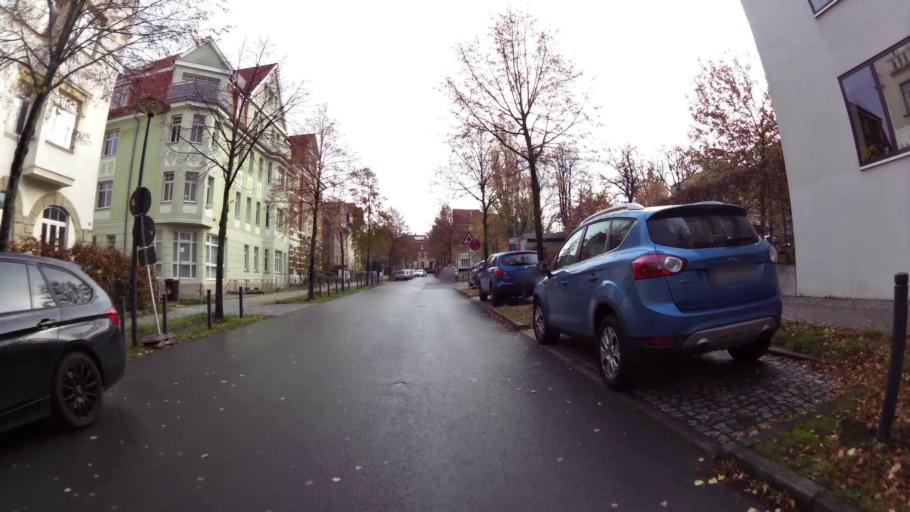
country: DE
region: Thuringia
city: Weimar
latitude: 50.9793
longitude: 11.3403
